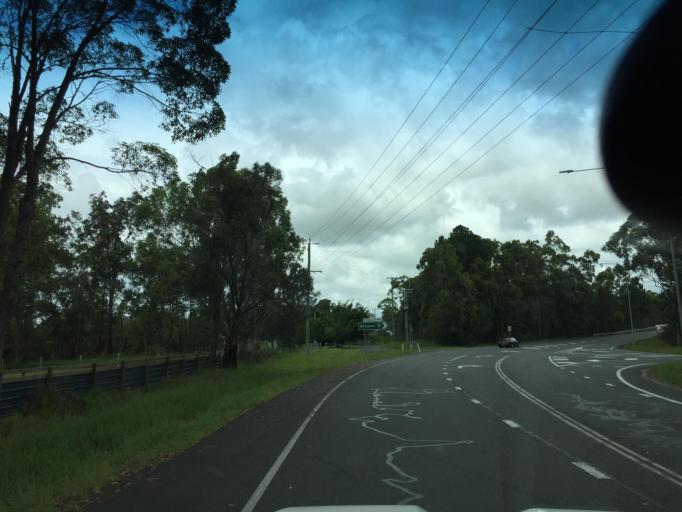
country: AU
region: Queensland
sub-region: Moreton Bay
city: Caboolture
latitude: -27.0592
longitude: 152.9103
